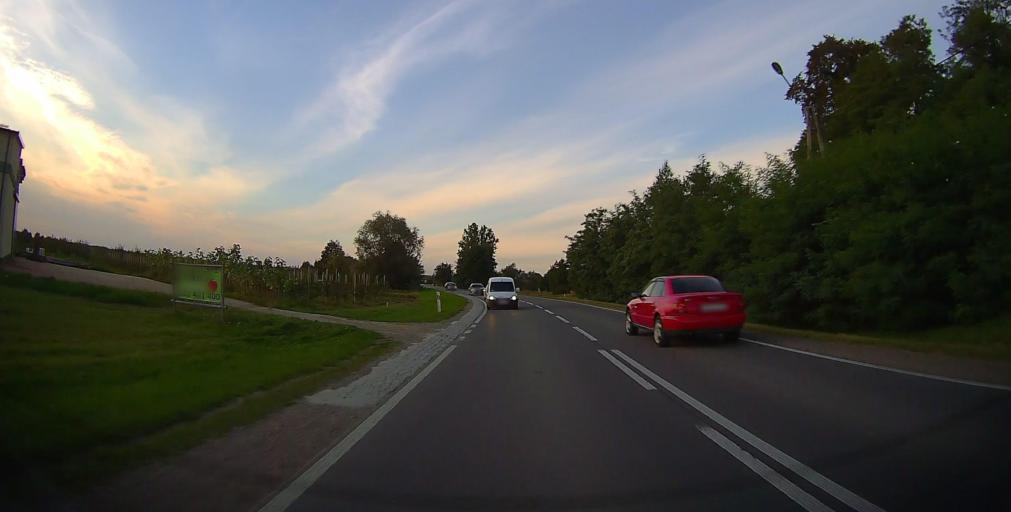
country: PL
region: Masovian Voivodeship
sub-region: Powiat garwolinski
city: Wilga
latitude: 51.7797
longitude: 21.3585
